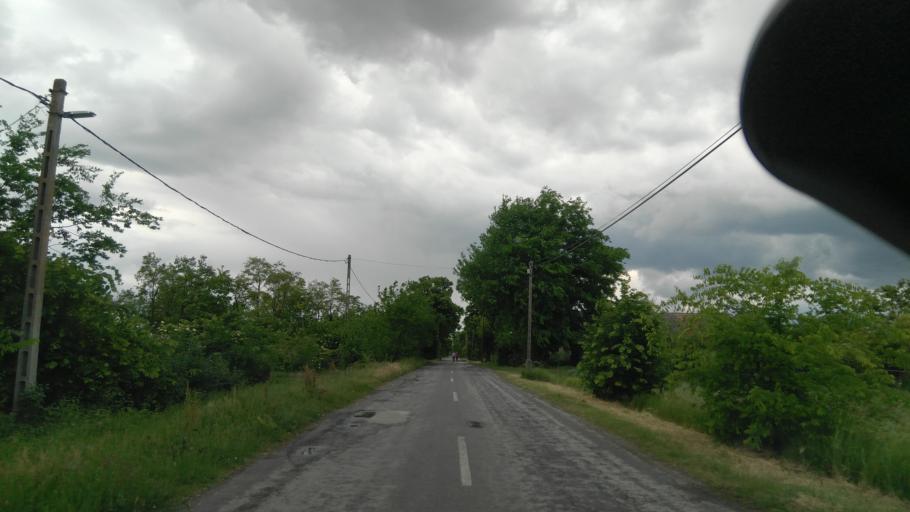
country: HU
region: Bekes
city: Gadoros
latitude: 46.6661
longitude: 20.5760
